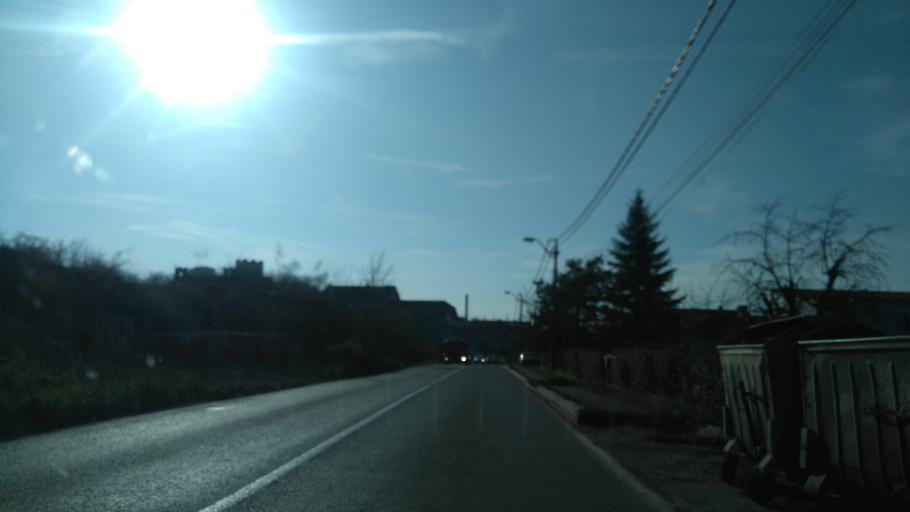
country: RS
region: Central Serbia
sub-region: Belgrade
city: Rakovica
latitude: 44.7375
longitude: 20.3851
